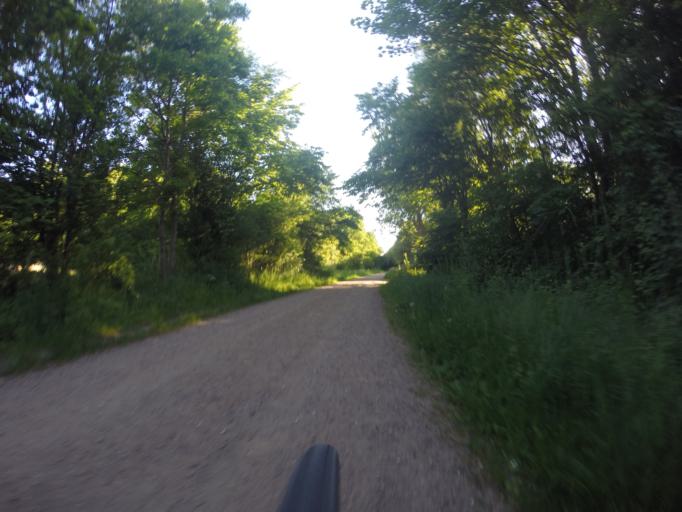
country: DK
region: Capital Region
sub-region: Albertslund Kommune
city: Albertslund
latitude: 55.6902
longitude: 12.3264
